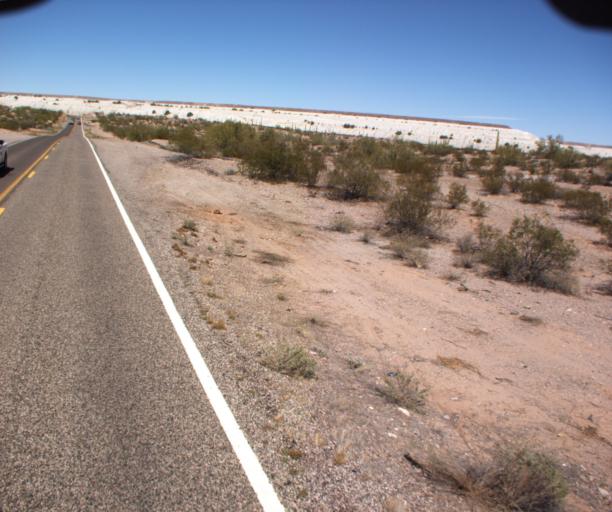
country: US
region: Arizona
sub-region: Pima County
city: Ajo
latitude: 32.3625
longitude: -112.8352
